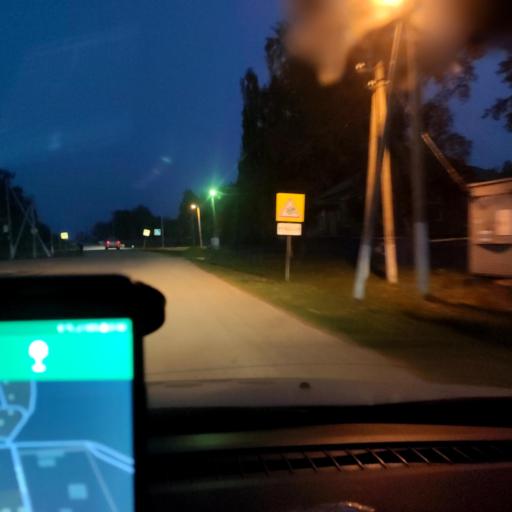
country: RU
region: Bashkortostan
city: Kabakovo
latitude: 54.6517
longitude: 56.3066
